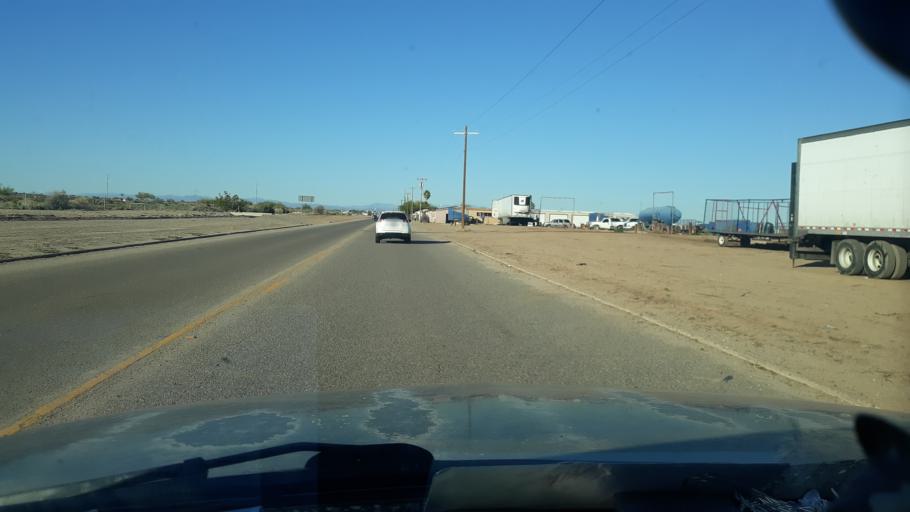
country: US
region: Arizona
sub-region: Maricopa County
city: Citrus Park
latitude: 33.5617
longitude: -112.3936
